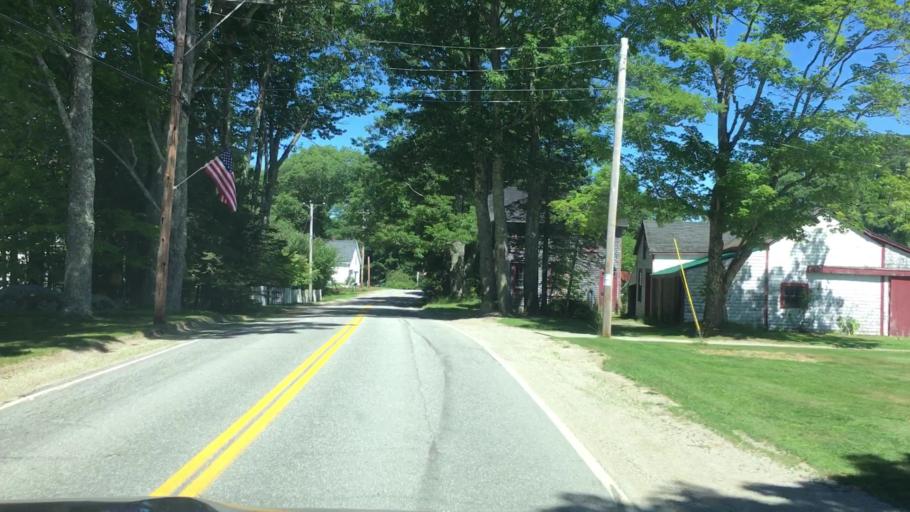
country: US
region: Maine
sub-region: Hancock County
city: Penobscot
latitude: 44.4556
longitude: -68.7029
